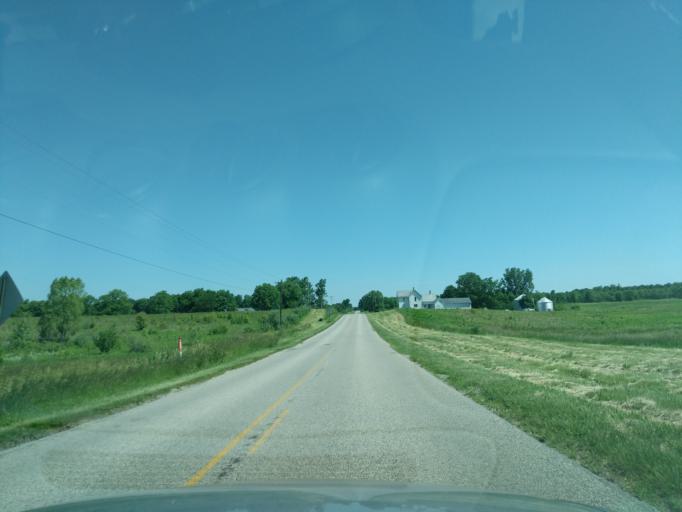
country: US
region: Indiana
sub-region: Huntington County
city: Huntington
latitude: 40.8305
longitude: -85.5086
